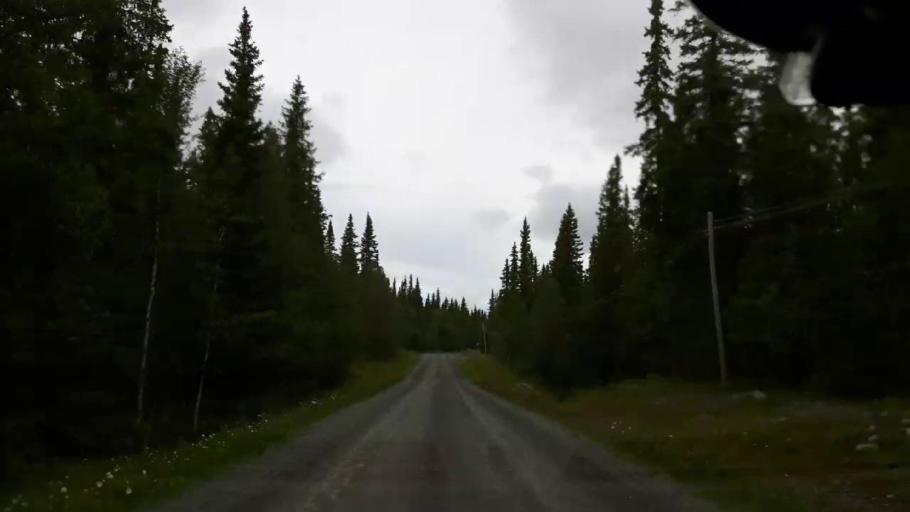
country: SE
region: Jaemtland
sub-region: Krokoms Kommun
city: Valla
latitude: 63.7118
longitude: 13.8620
